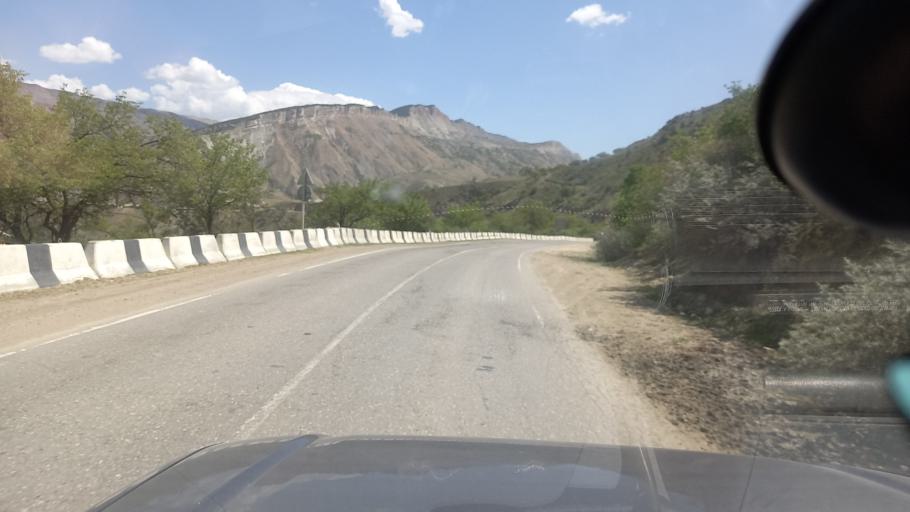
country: RU
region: Dagestan
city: Gunib
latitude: 42.4309
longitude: 46.9896
